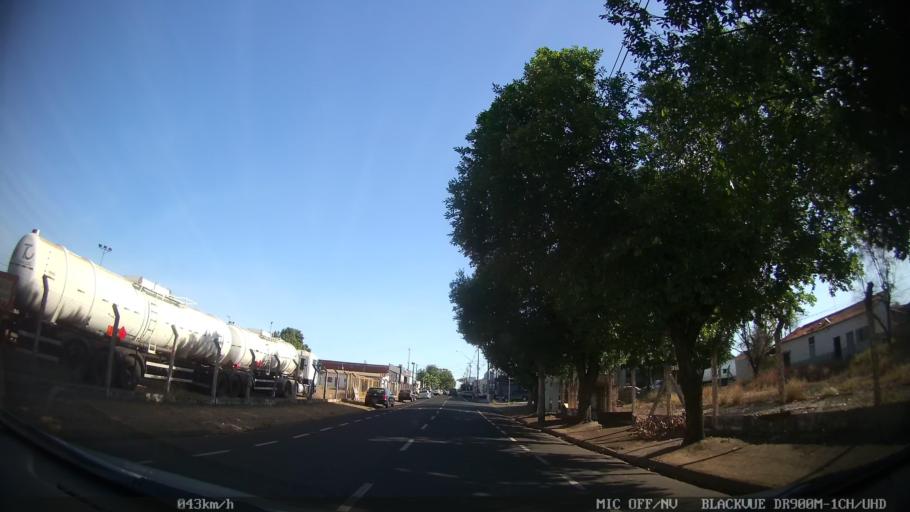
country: BR
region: Sao Paulo
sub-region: Sao Jose Do Rio Preto
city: Sao Jose do Rio Preto
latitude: -20.7854
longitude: -49.3547
